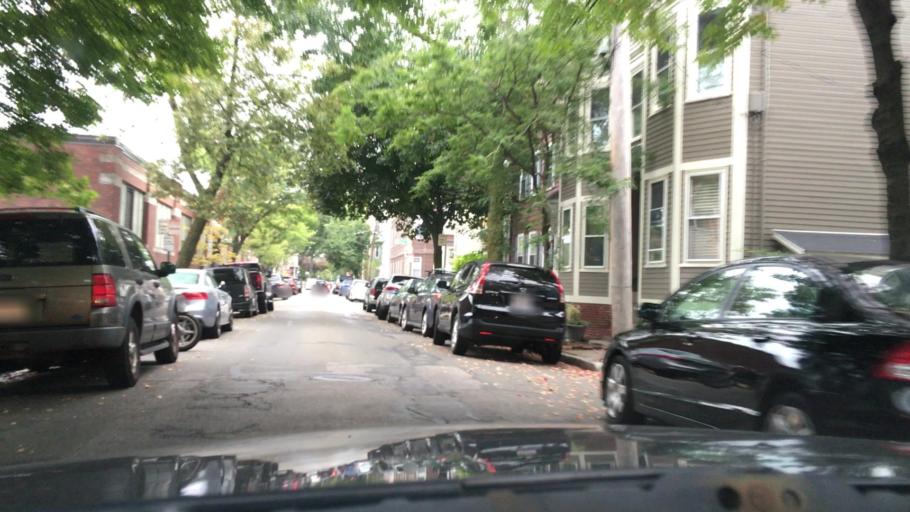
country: US
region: Massachusetts
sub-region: Middlesex County
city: Cambridge
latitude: 42.3727
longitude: -71.0974
